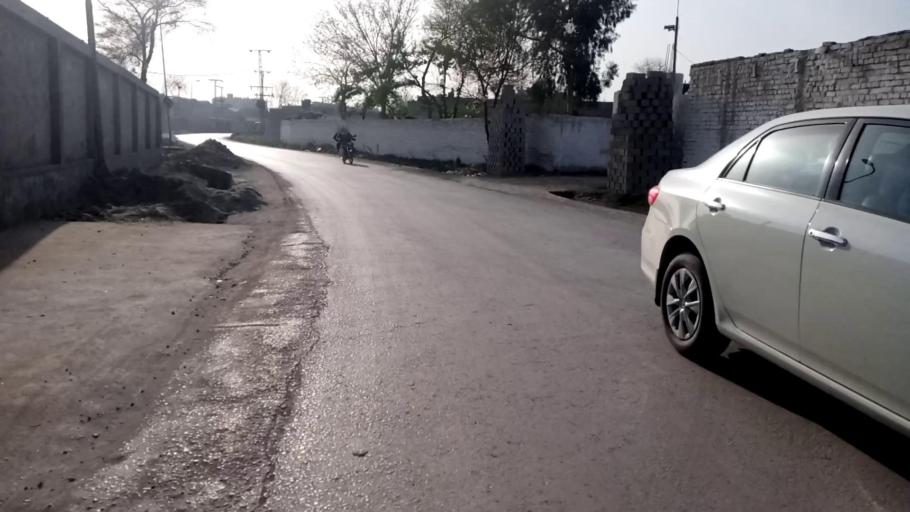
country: PK
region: Khyber Pakhtunkhwa
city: Peshawar
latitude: 33.9967
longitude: 71.4317
